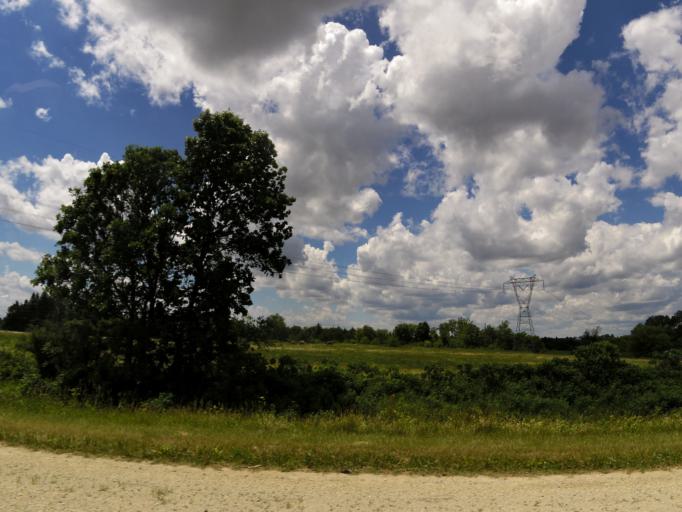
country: US
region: Iowa
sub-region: Fayette County
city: Oelwein
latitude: 42.5915
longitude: -91.9023
